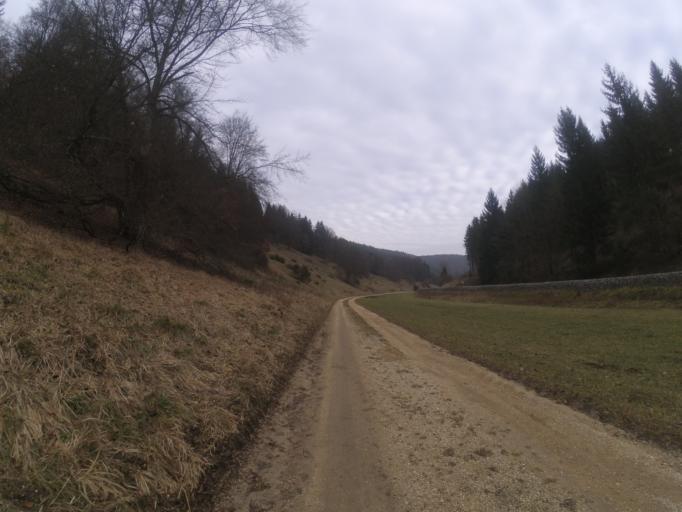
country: DE
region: Baden-Wuerttemberg
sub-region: Tuebingen Region
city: Mehrstetten
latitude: 48.3558
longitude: 9.5671
